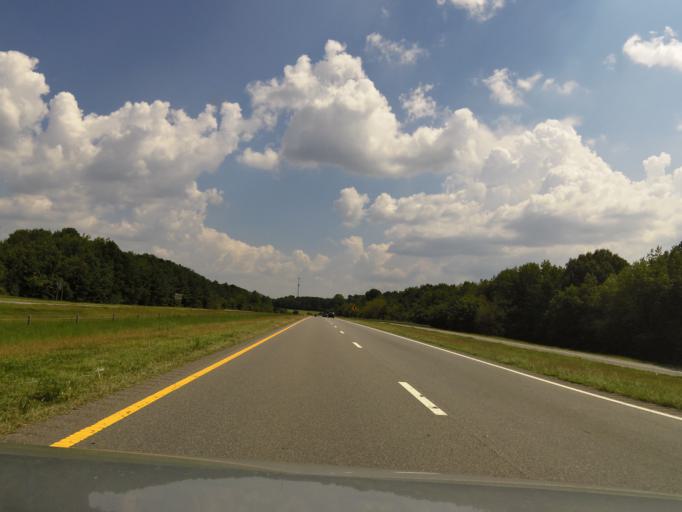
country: US
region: North Carolina
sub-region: Cleveland County
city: Kings Mountain
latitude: 35.2462
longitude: -81.3287
